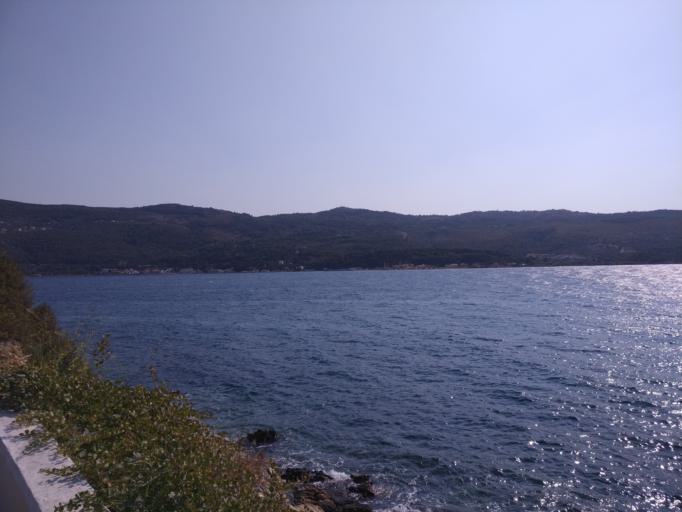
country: GR
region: North Aegean
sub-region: Nomos Samou
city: Samos
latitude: 37.7645
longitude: 26.9652
